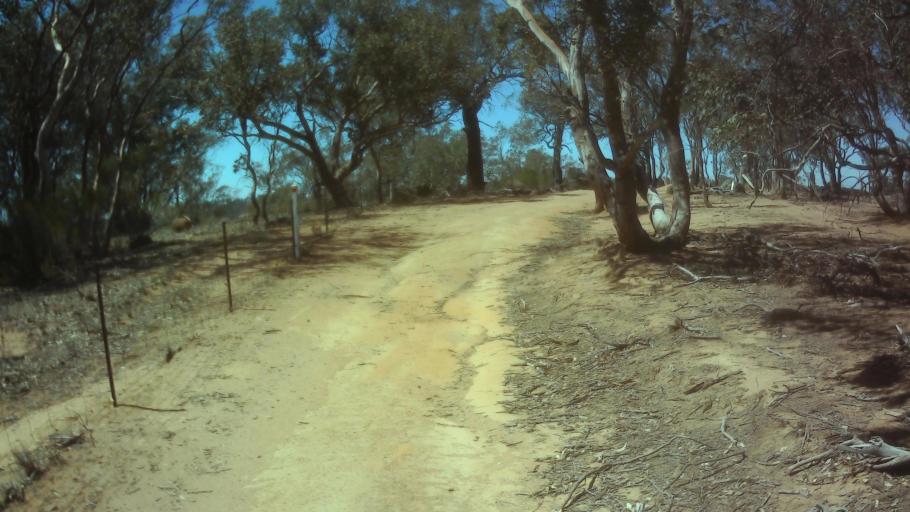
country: AU
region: New South Wales
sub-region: Cowra
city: Cowra
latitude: -33.9045
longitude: 148.5093
